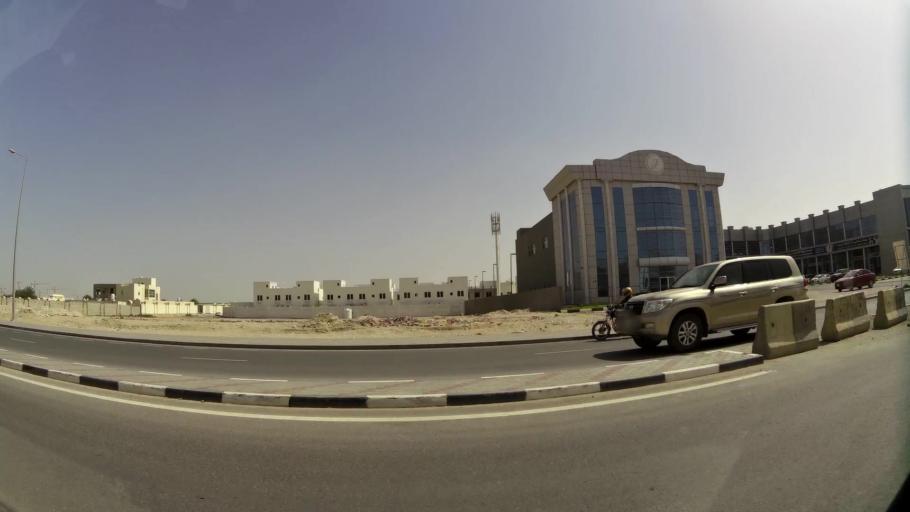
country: QA
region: Baladiyat Umm Salal
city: Umm Salal Muhammad
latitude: 25.4089
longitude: 51.4192
